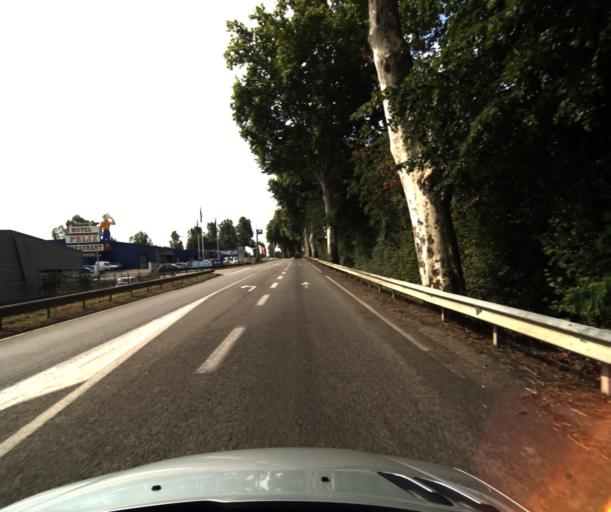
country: FR
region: Midi-Pyrenees
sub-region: Departement du Tarn-et-Garonne
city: Moissac
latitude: 44.0760
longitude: 1.0927
